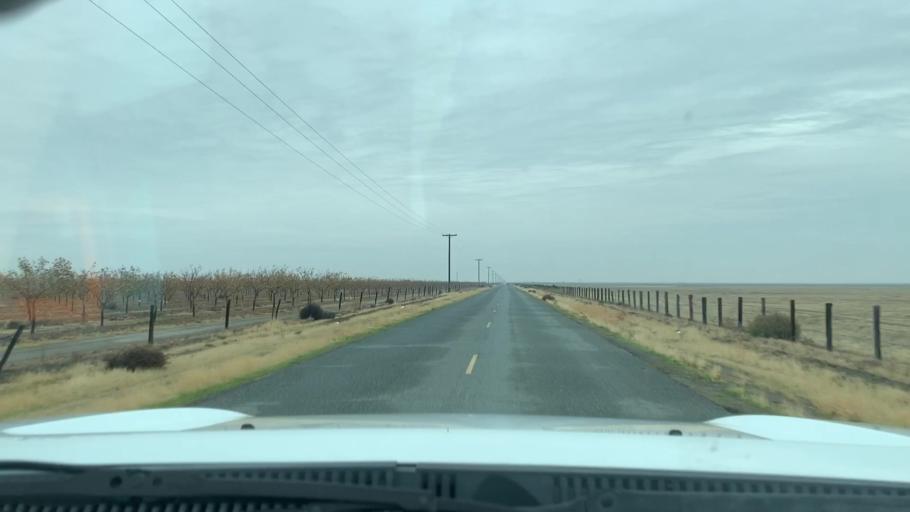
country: US
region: California
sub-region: Tulare County
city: Alpaugh
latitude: 35.7608
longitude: -119.5601
